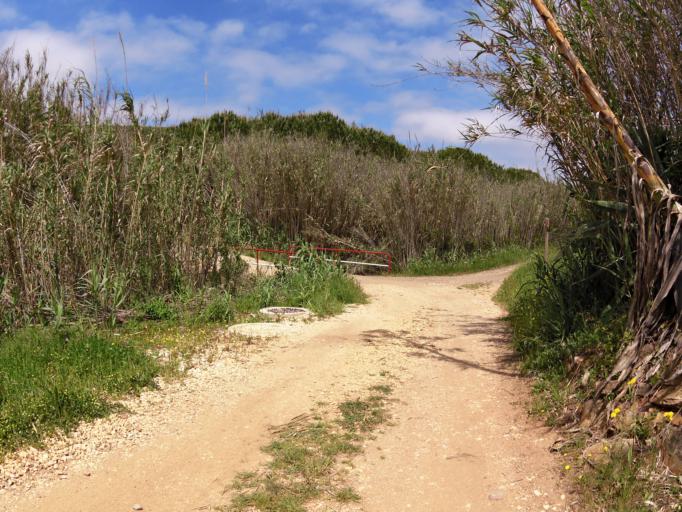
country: PT
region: Faro
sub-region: Vila do Bispo
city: Vila do Bispo
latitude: 37.0737
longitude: -8.8741
